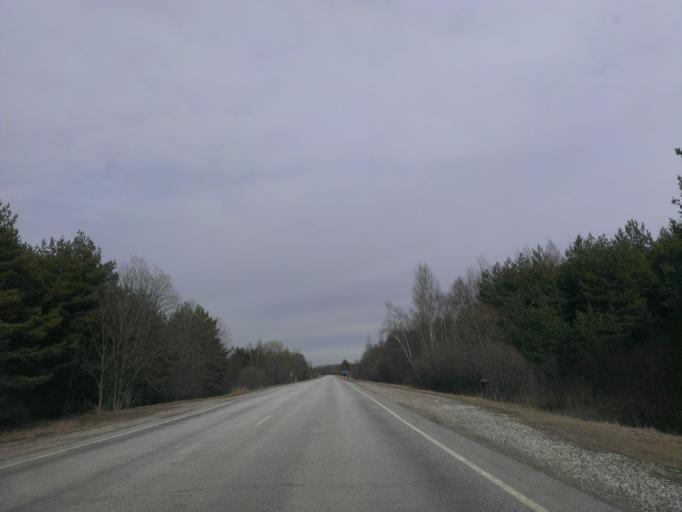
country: EE
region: Laeaene
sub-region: Lihula vald
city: Lihula
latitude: 58.5924
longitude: 23.5411
